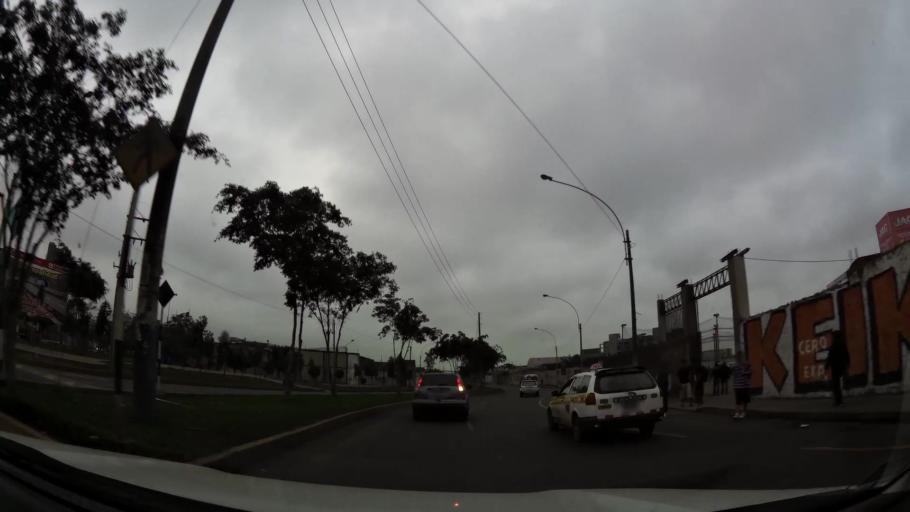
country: PE
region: Lima
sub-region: Lima
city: San Luis
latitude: -12.0626
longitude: -76.9777
